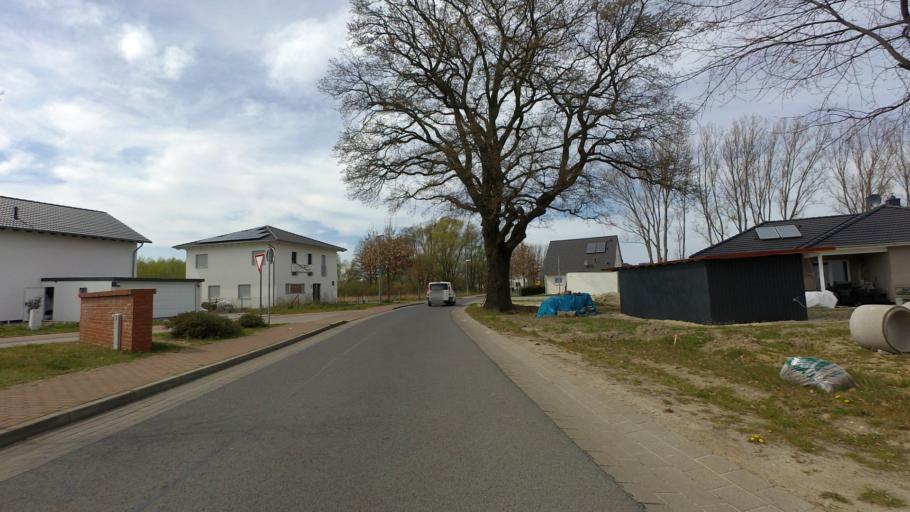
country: DE
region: Brandenburg
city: Schonefeld
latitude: 52.3394
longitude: 13.5246
